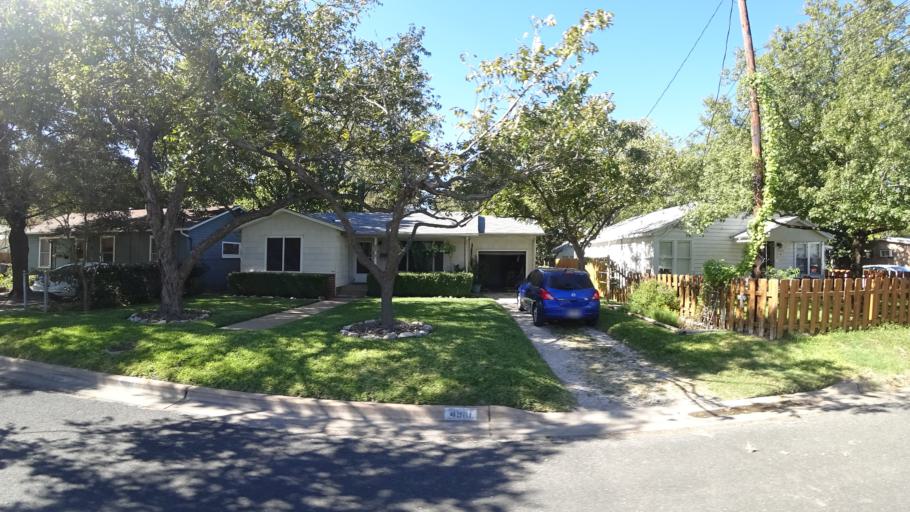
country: US
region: Texas
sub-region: Travis County
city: Austin
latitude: 30.3203
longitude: -97.7371
